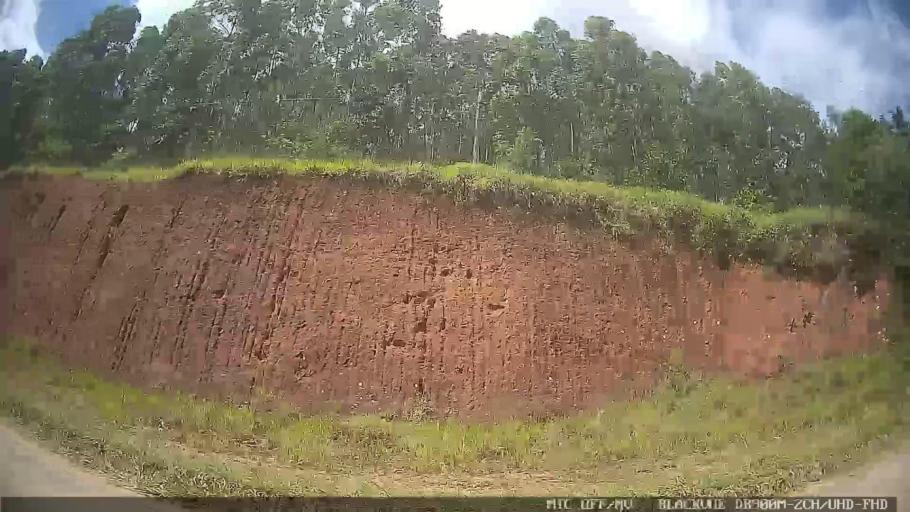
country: BR
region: Minas Gerais
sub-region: Extrema
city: Extrema
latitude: -22.8064
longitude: -46.4624
